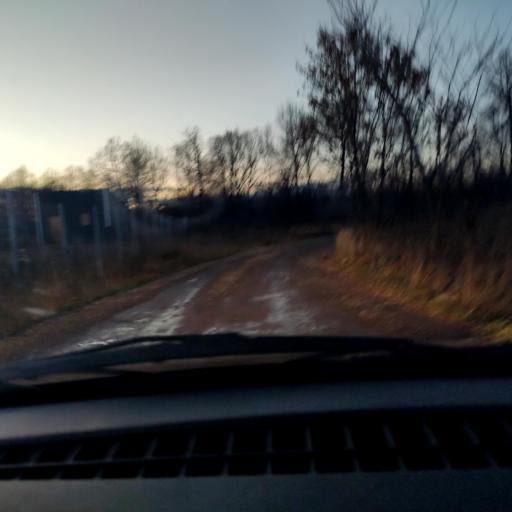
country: RU
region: Bashkortostan
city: Ufa
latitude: 54.6555
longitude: 55.8868
